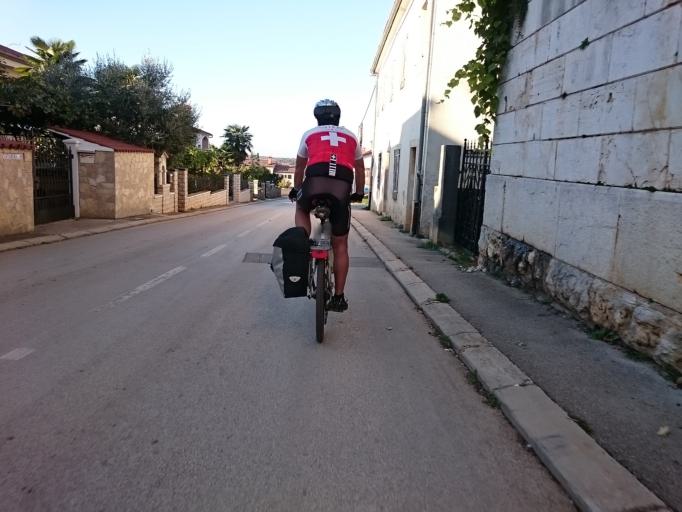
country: HR
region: Istarska
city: Novigrad
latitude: 45.3026
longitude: 13.6250
